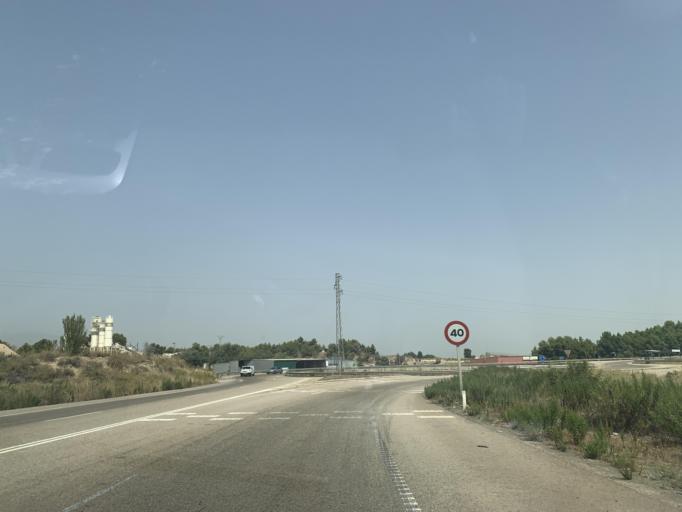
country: ES
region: Aragon
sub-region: Provincia de Zaragoza
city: Zaragoza
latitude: 41.5983
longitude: -0.8359
